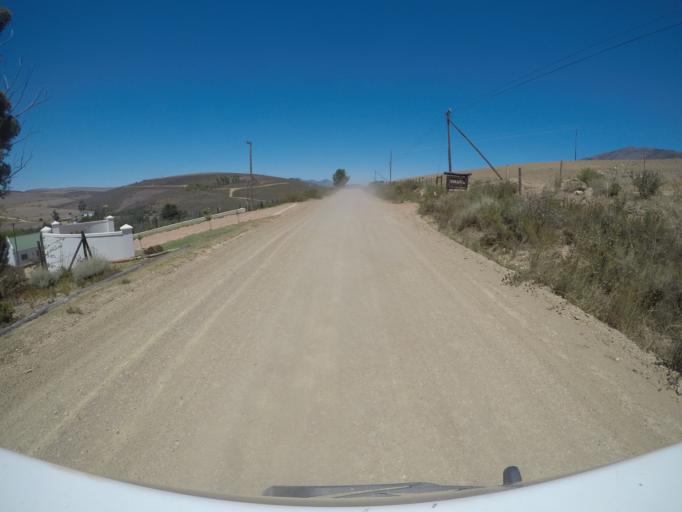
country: ZA
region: Western Cape
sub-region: Overberg District Municipality
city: Caledon
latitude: -34.1756
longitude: 19.2258
